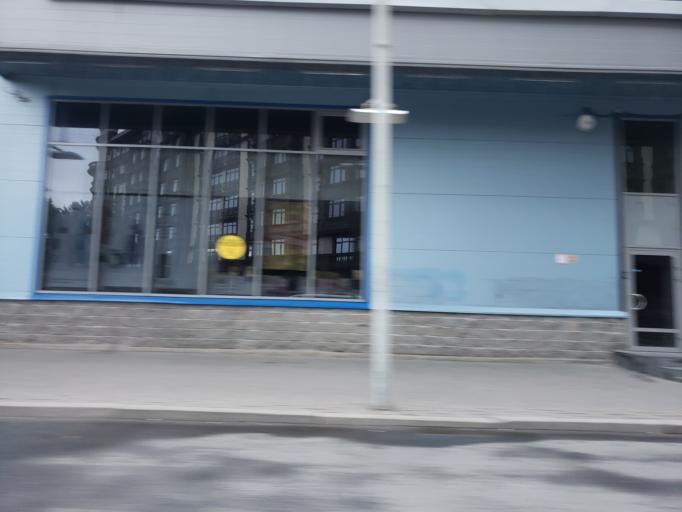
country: RU
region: St.-Petersburg
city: Vasyl'evsky Ostrov
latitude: 59.9386
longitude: 30.2305
